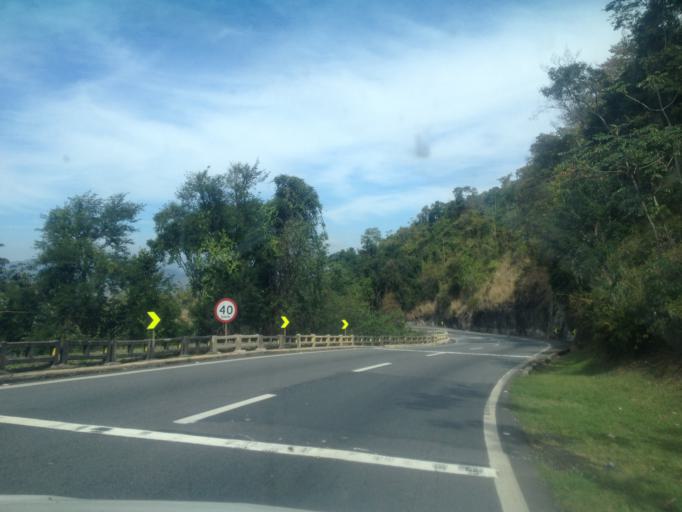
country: BR
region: Rio de Janeiro
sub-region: Pirai
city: Pirai
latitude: -22.6705
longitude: -43.8281
